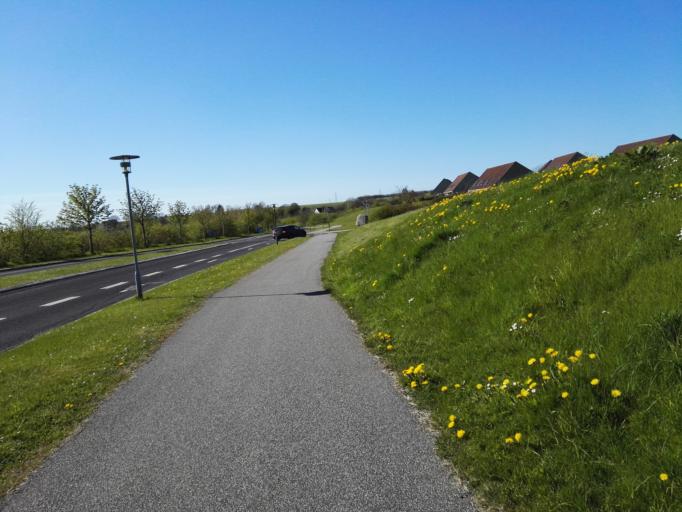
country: DK
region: Capital Region
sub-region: Egedal Kommune
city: Vekso
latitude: 55.7514
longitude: 12.2329
